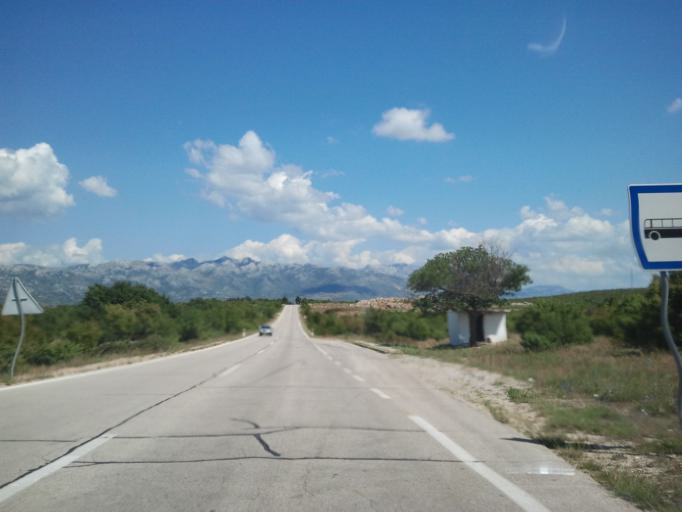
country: HR
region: Zadarska
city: Krusevo
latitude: 44.1929
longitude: 15.6437
